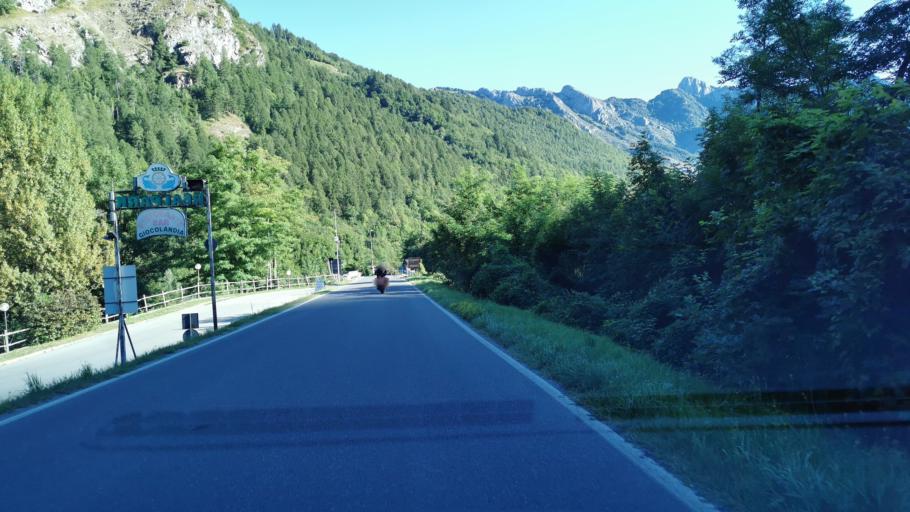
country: IT
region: Piedmont
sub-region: Provincia di Cuneo
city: Valdieri
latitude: 44.2619
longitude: 7.3815
